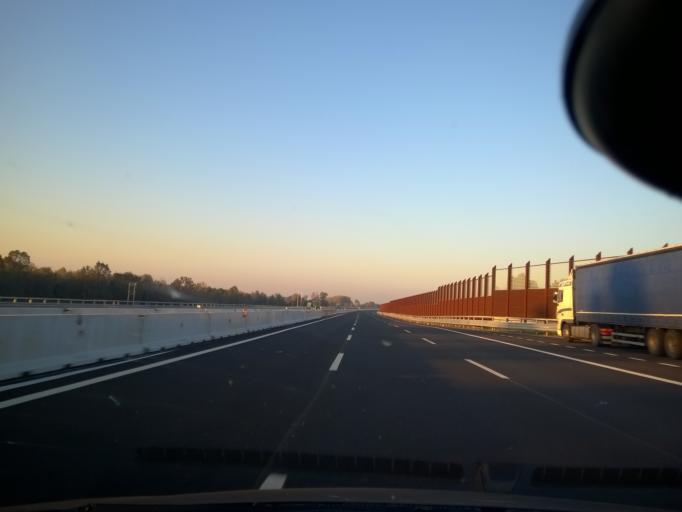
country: IT
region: Lombardy
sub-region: Provincia di Lodi
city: Cassino d'Alberi
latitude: 45.3812
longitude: 9.3754
